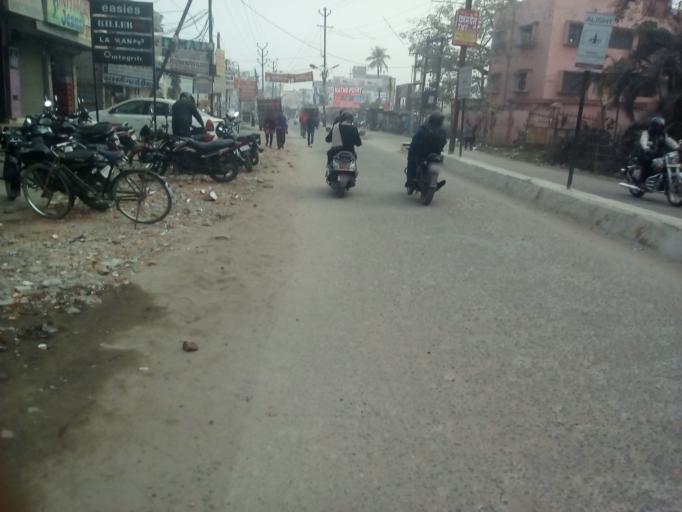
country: IN
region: Bihar
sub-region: Muzaffarpur
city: Muzaffarpur
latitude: 26.1094
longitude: 85.3962
